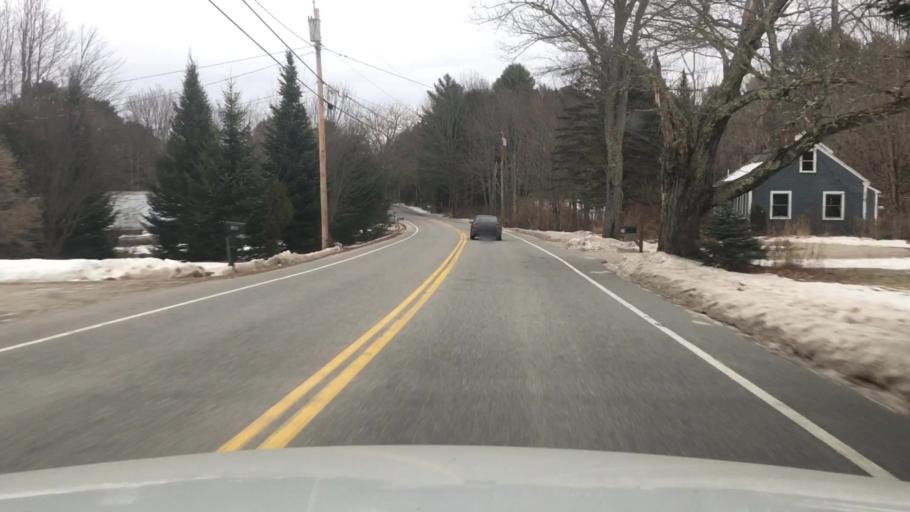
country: US
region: Maine
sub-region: Cumberland County
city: Freeport
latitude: 43.8748
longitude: -70.0597
